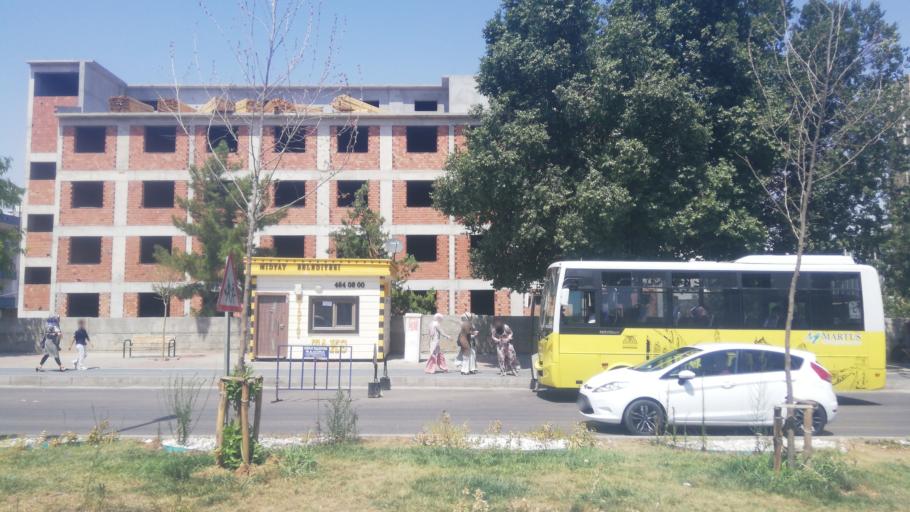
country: TR
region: Mardin
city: Midyat
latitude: 37.4153
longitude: 41.3723
